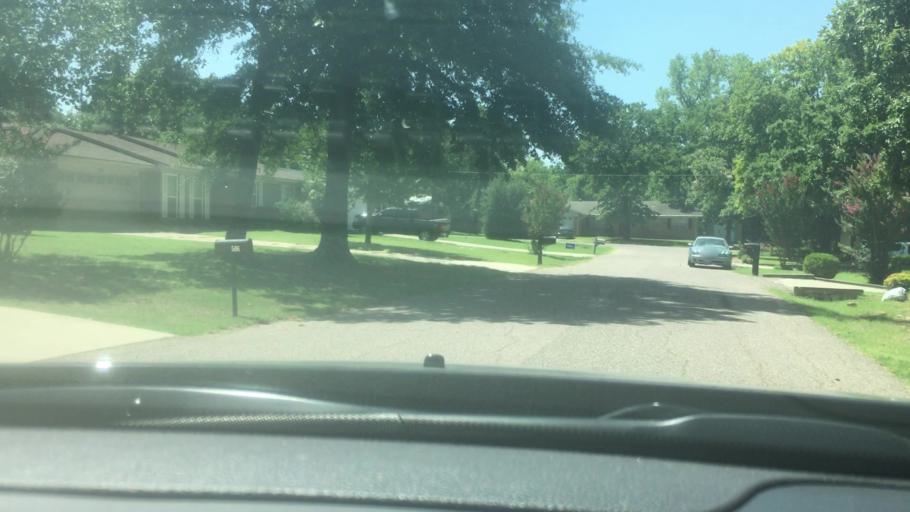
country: US
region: Oklahoma
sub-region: Pontotoc County
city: Ada
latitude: 34.7796
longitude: -96.6381
